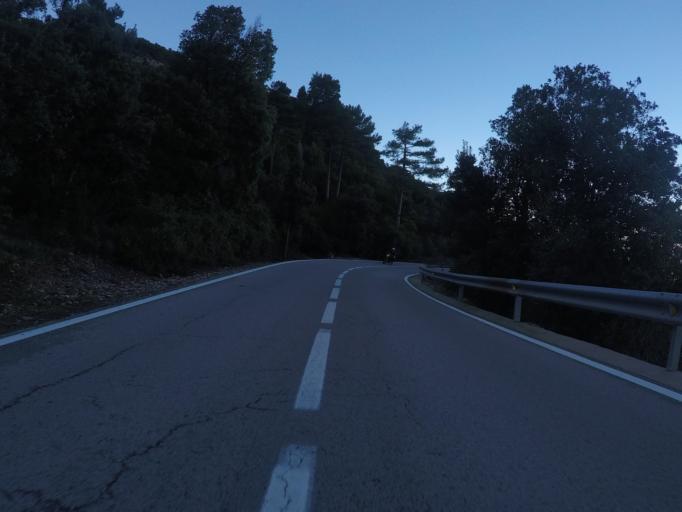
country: ES
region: Catalonia
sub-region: Provincia de Barcelona
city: Monistrol de Montserrat
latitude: 41.6062
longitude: 1.8260
